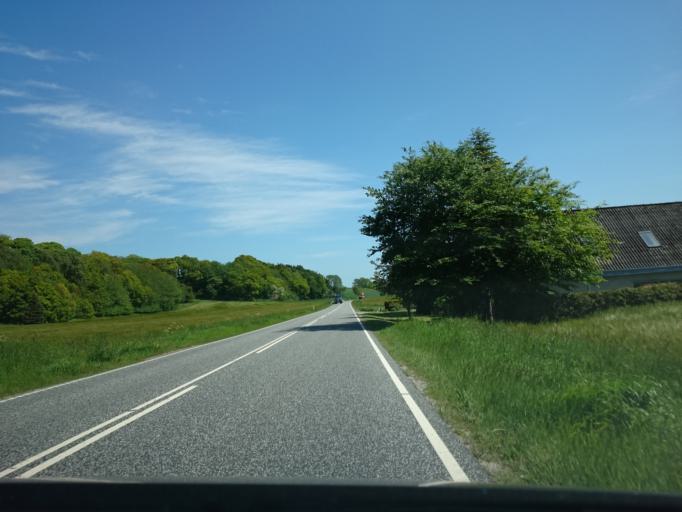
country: DK
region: Central Jutland
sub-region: Randers Kommune
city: Assentoft
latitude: 56.4051
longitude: 10.1353
